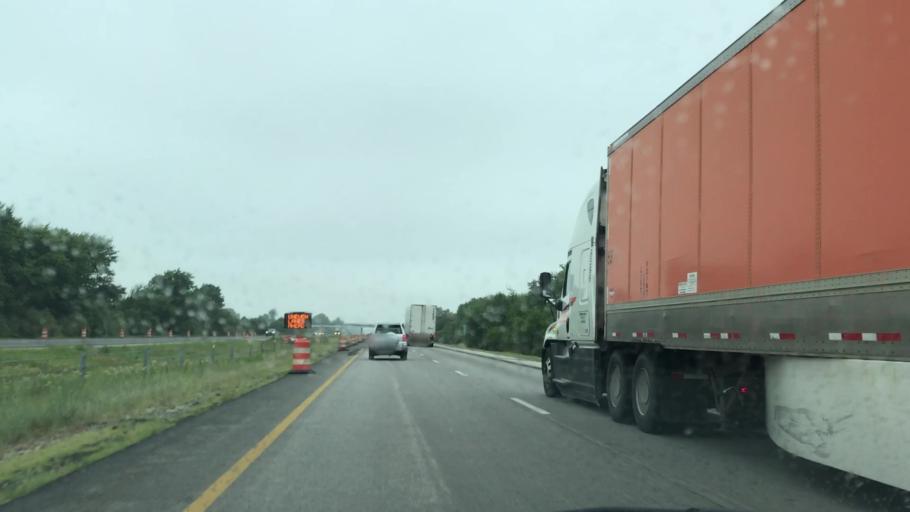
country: US
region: Indiana
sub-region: Clinton County
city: Mulberry
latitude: 40.2723
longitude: -86.6699
